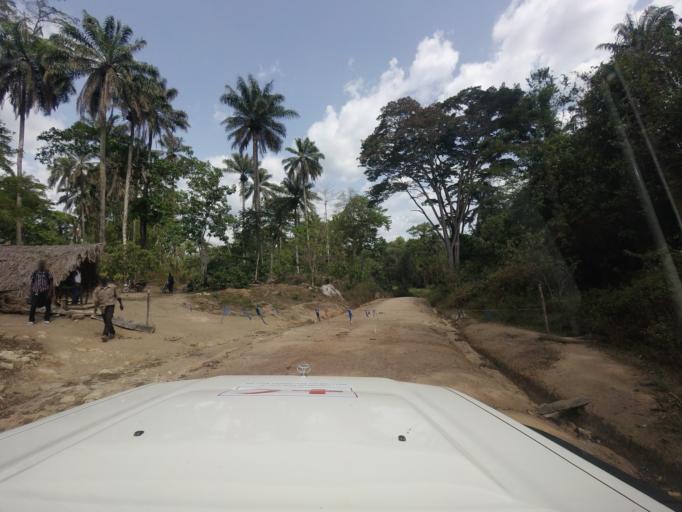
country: LR
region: Lofa
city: Voinjama
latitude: 8.4049
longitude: -9.6604
